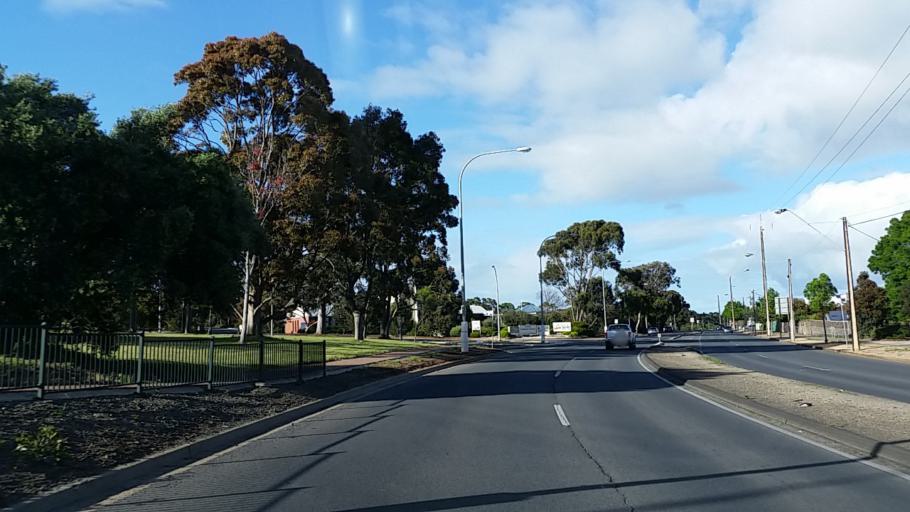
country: AU
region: South Australia
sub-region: Mitcham
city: Clapham
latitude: -34.9994
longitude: 138.5931
